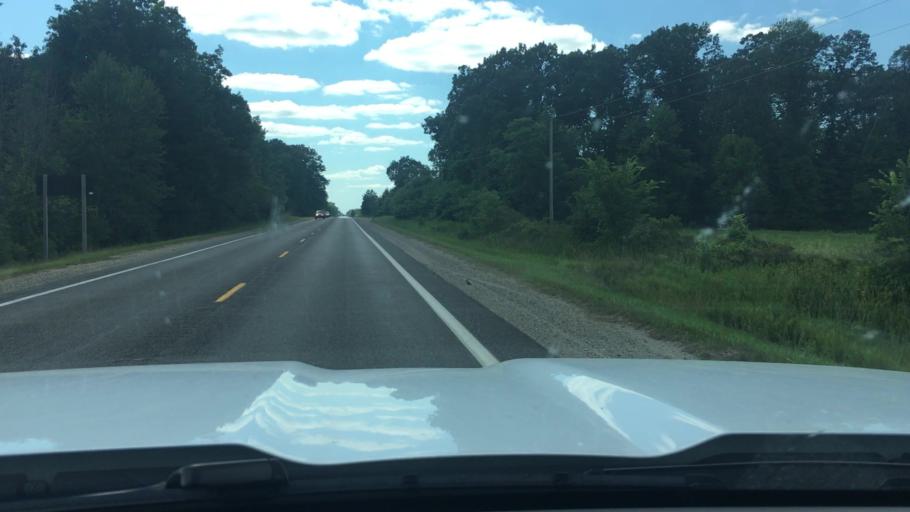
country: US
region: Michigan
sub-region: Clinton County
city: Ovid
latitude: 43.1760
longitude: -84.3908
